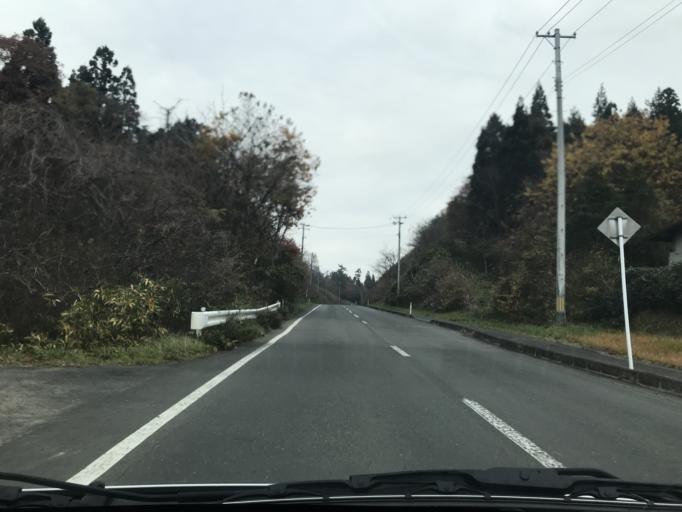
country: JP
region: Iwate
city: Mizusawa
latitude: 39.1641
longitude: 141.2037
